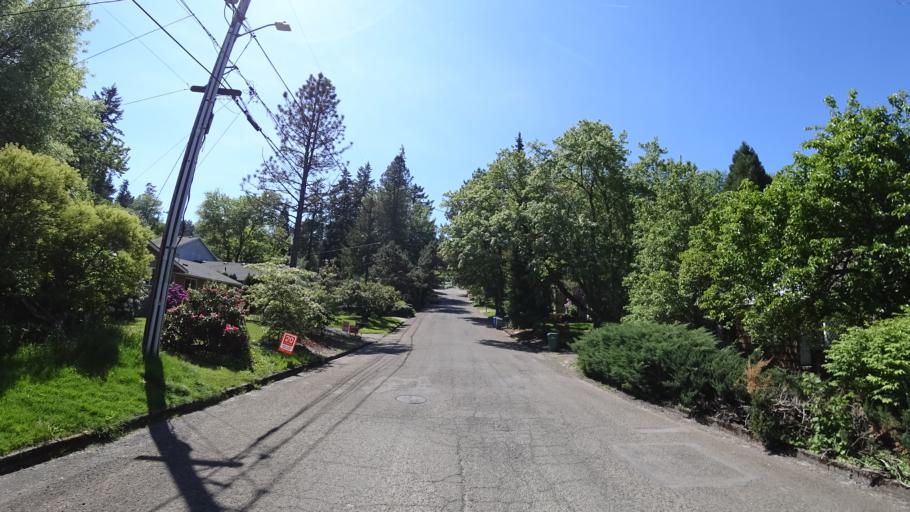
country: US
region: Oregon
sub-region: Washington County
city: Metzger
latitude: 45.4468
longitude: -122.7175
